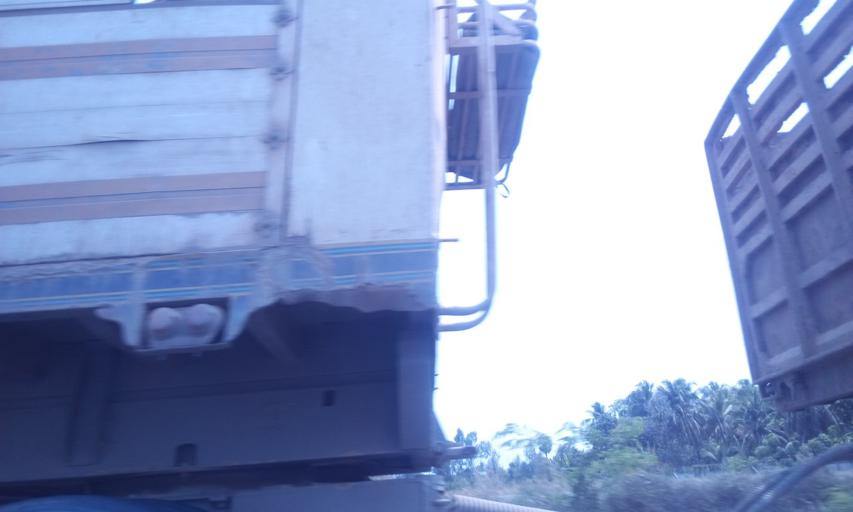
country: TH
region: Chachoengsao
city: Bang Nam Priao
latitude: 13.8968
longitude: 100.9715
